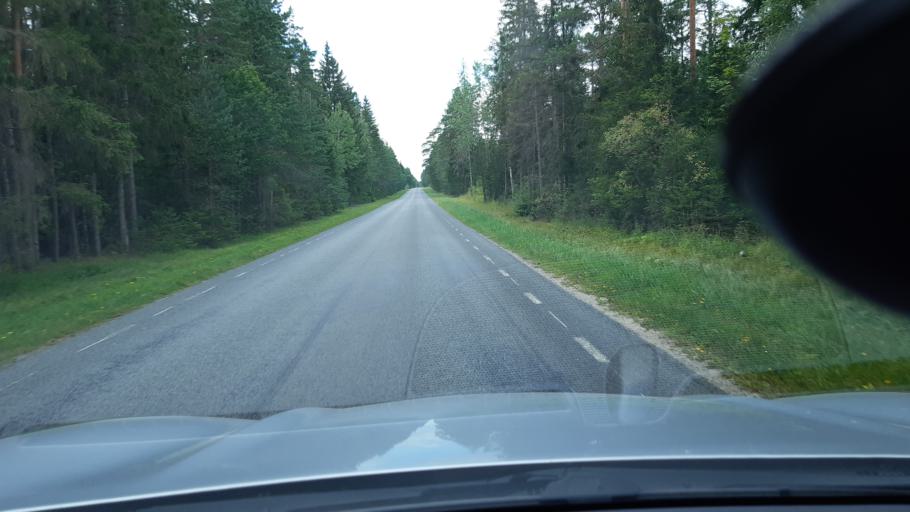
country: EE
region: Raplamaa
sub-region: Rapla vald
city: Rapla
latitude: 58.8990
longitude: 24.6945
